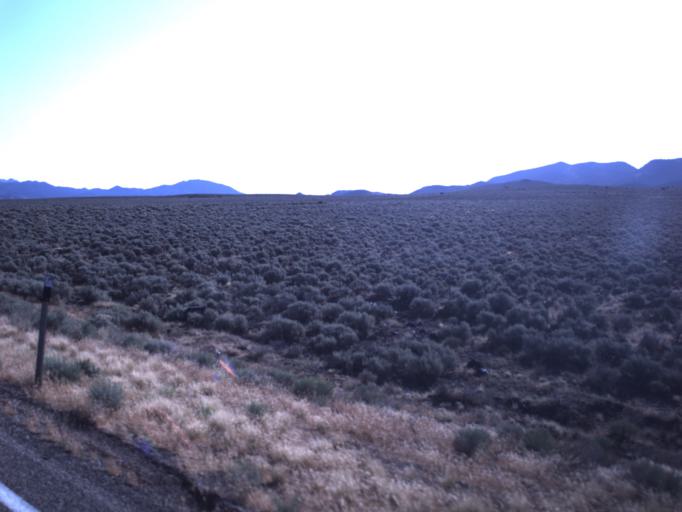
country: US
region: Utah
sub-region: Beaver County
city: Milford
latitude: 38.1564
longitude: -112.9577
